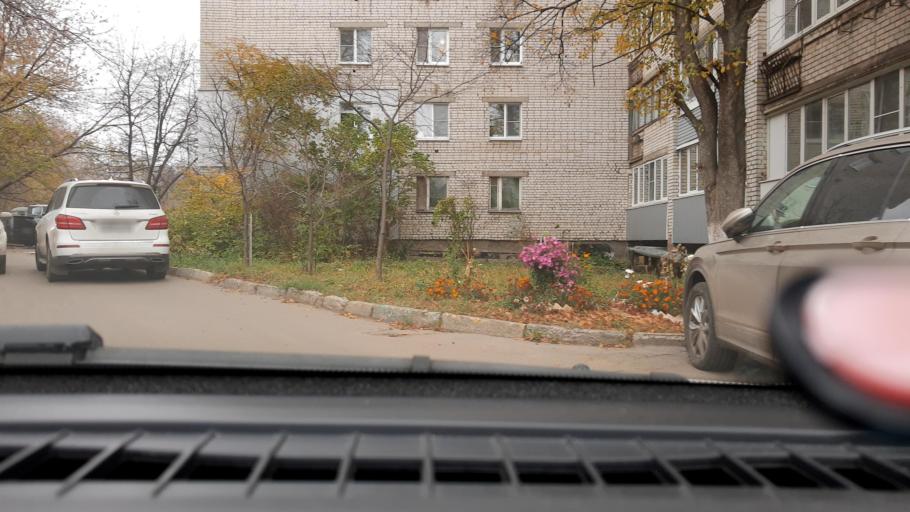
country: RU
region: Nizjnij Novgorod
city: Nizhniy Novgorod
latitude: 56.2753
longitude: 43.9912
